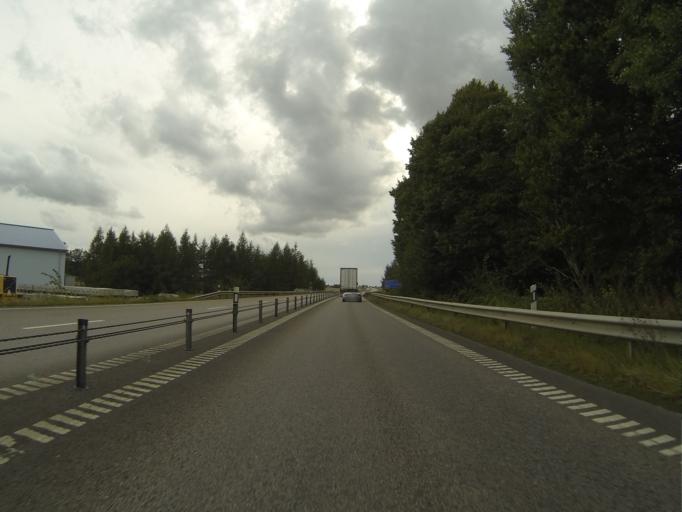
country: SE
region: Skane
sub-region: Horby Kommun
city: Hoerby
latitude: 55.8485
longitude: 13.6000
